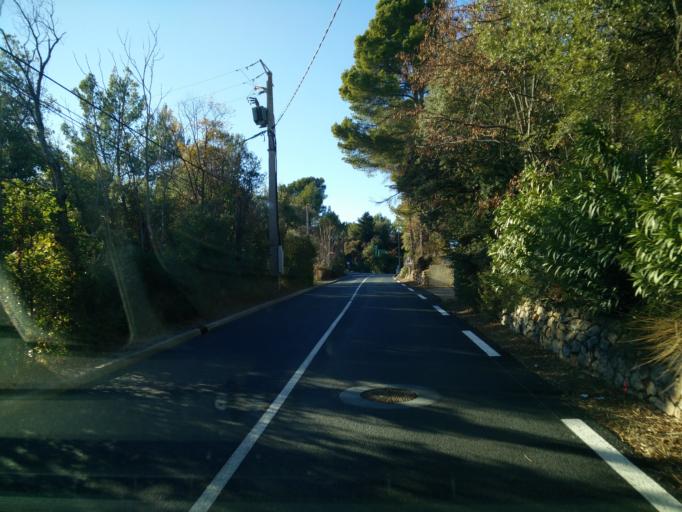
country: FR
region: Provence-Alpes-Cote d'Azur
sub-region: Departement du Var
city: Villecroze
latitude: 43.5839
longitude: 6.2722
